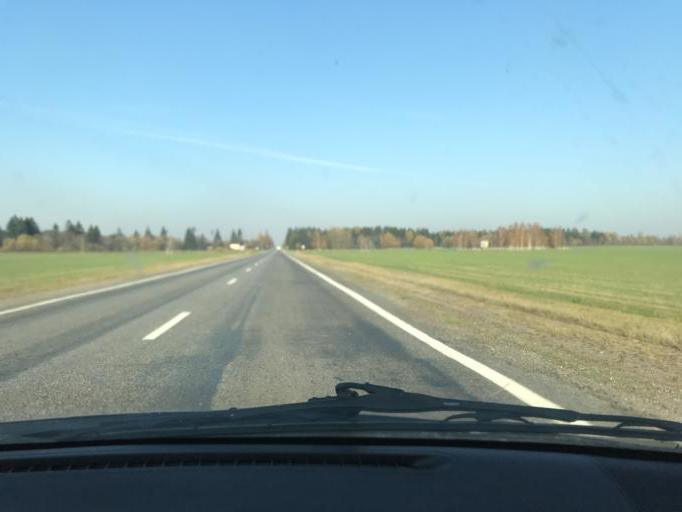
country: BY
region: Vitebsk
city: Orsha
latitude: 54.4471
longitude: 30.4893
